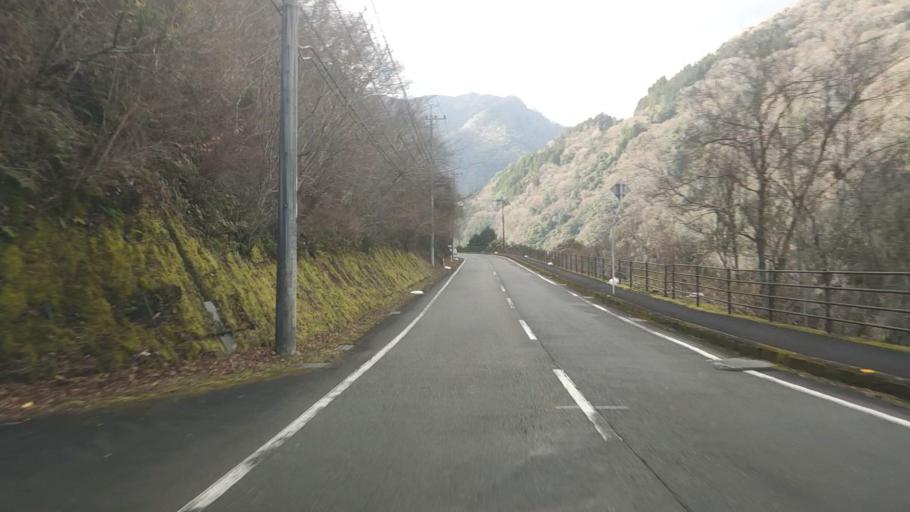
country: JP
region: Kumamoto
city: Hitoyoshi
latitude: 32.4070
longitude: 130.8280
